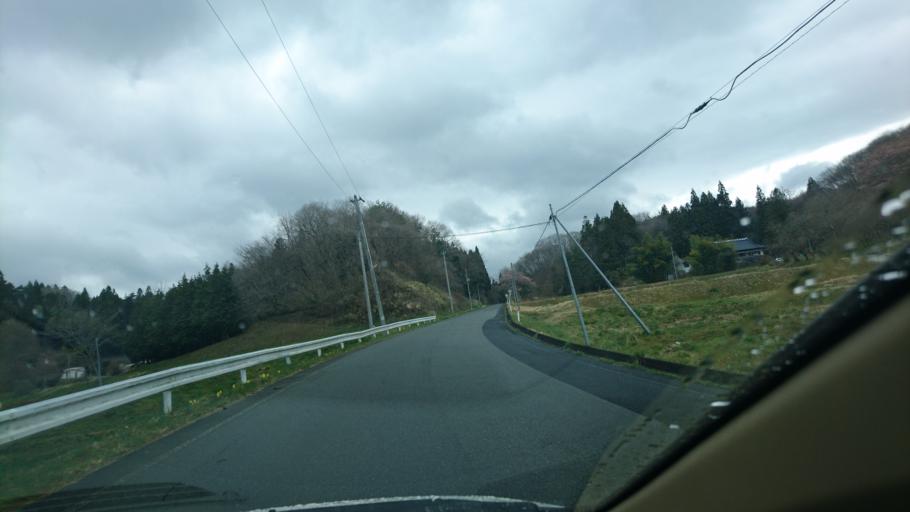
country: JP
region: Iwate
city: Ichinoseki
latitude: 38.9480
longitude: 141.3191
